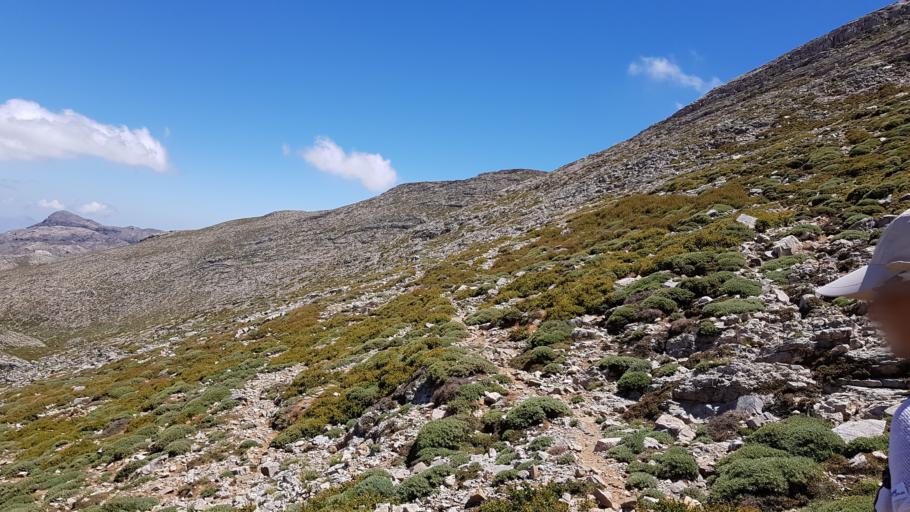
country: GR
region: Crete
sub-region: Nomos Rethymnis
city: Zoniana
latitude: 35.2087
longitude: 24.7980
